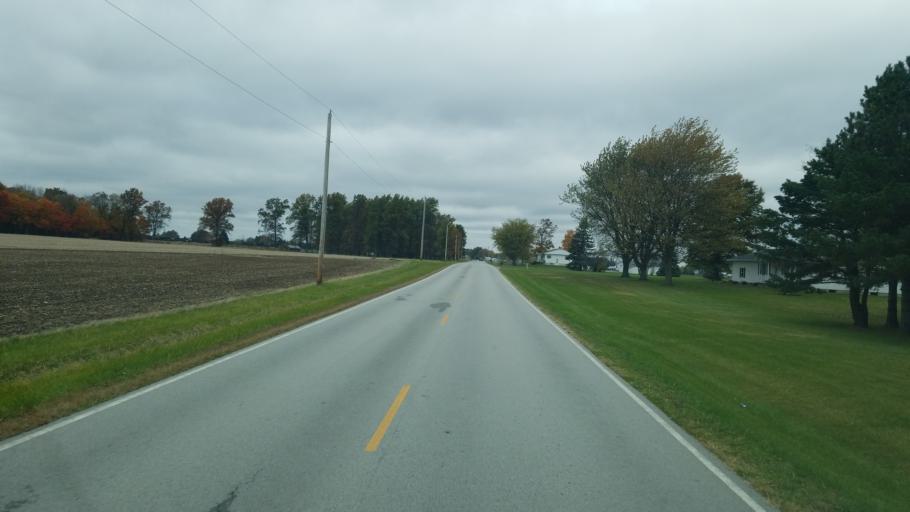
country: US
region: Ohio
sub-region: Huron County
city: Willard
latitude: 41.0426
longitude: -82.8846
